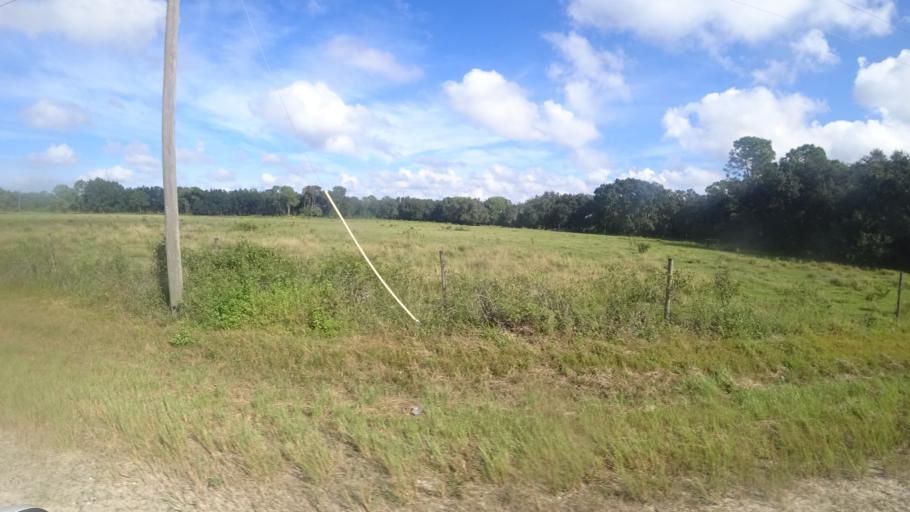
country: US
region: Florida
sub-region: Hillsborough County
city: Ruskin
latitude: 27.6136
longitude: -82.4103
